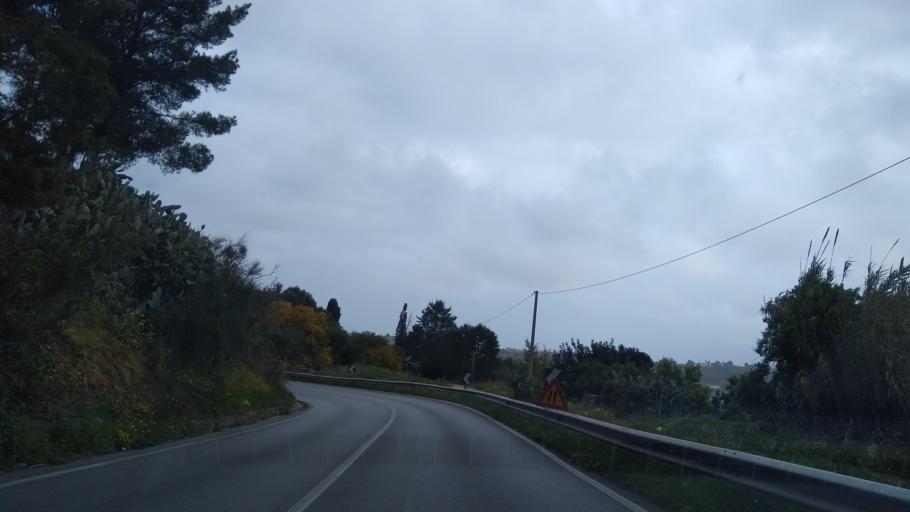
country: IT
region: Sicily
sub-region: Trapani
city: Alcamo
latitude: 37.9781
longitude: 12.9386
